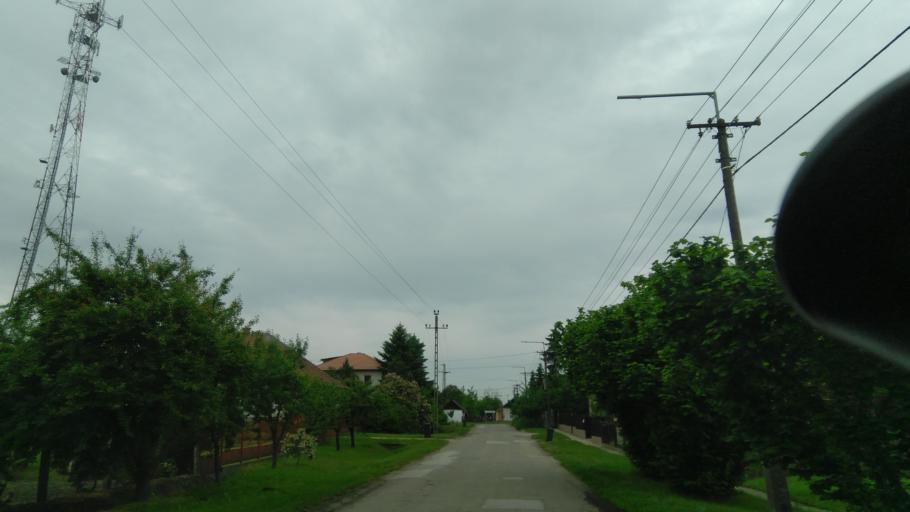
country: HU
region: Bekes
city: Fuzesgyarmat
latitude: 47.1000
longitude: 21.2071
